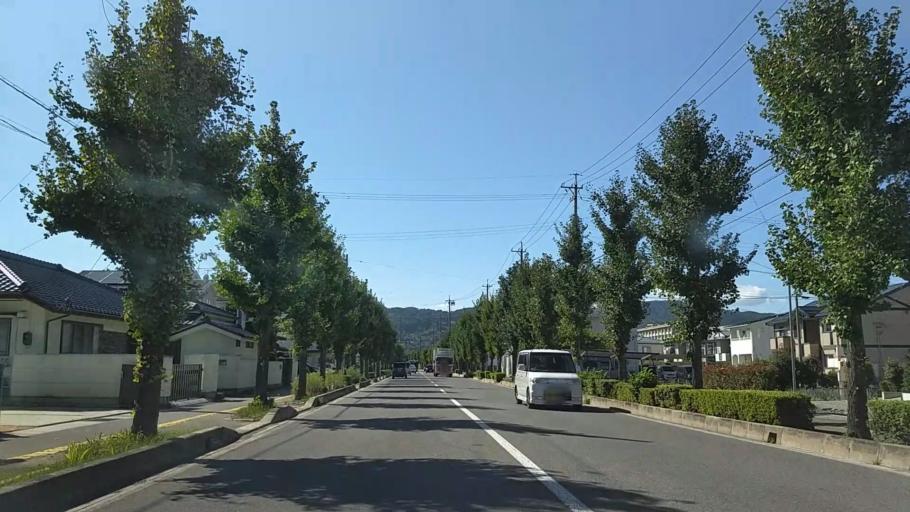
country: JP
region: Nagano
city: Nagano-shi
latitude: 36.5821
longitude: 138.1462
